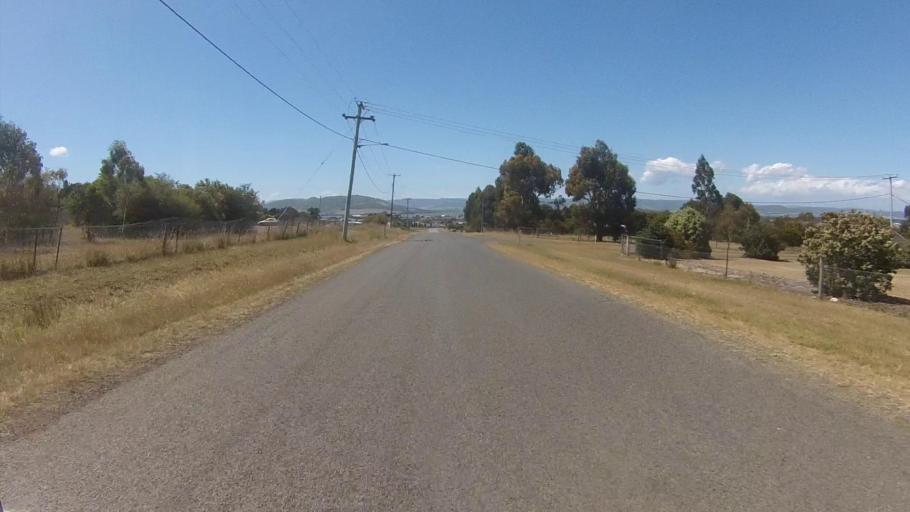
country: AU
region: Tasmania
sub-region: Clarence
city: Cambridge
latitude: -42.8474
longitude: 147.4639
